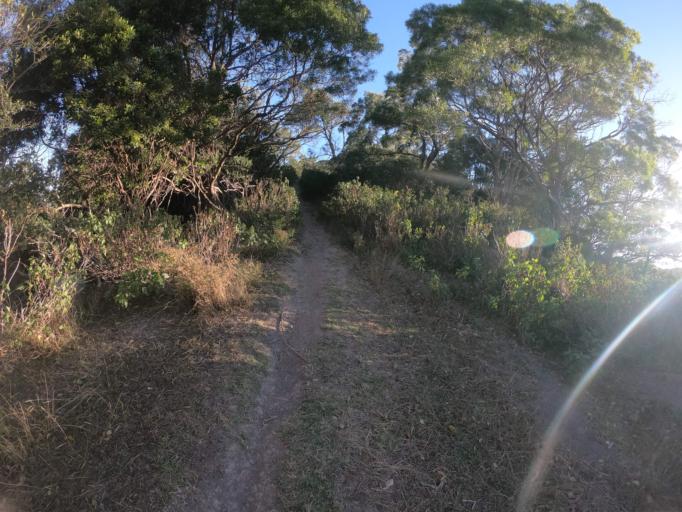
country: AU
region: New South Wales
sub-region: Wollongong
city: Mount Keira
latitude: -34.4189
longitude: 150.8418
